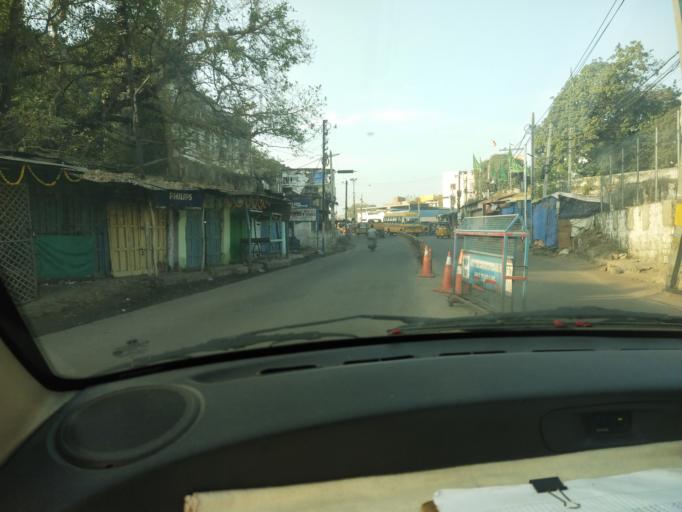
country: IN
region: Telangana
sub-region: Hyderabad
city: Hyderabad
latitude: 17.3692
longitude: 78.4584
